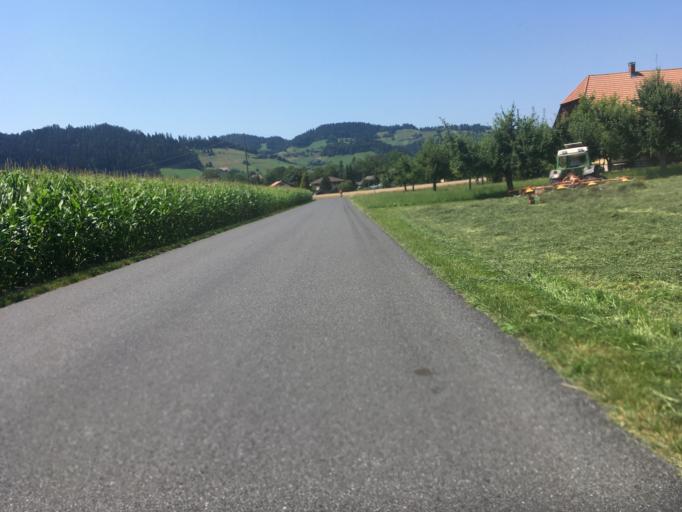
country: CH
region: Bern
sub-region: Emmental District
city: Lauperswil
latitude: 46.9474
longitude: 7.7555
